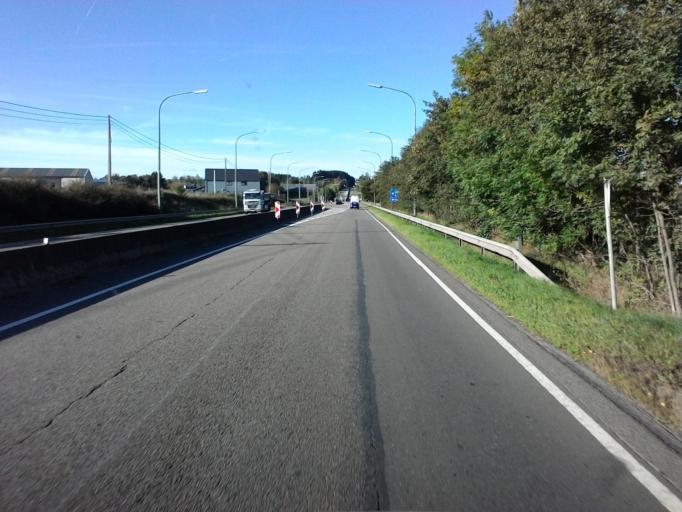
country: BE
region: Wallonia
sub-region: Province du Luxembourg
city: Fauvillers
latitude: 49.9018
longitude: 5.7004
